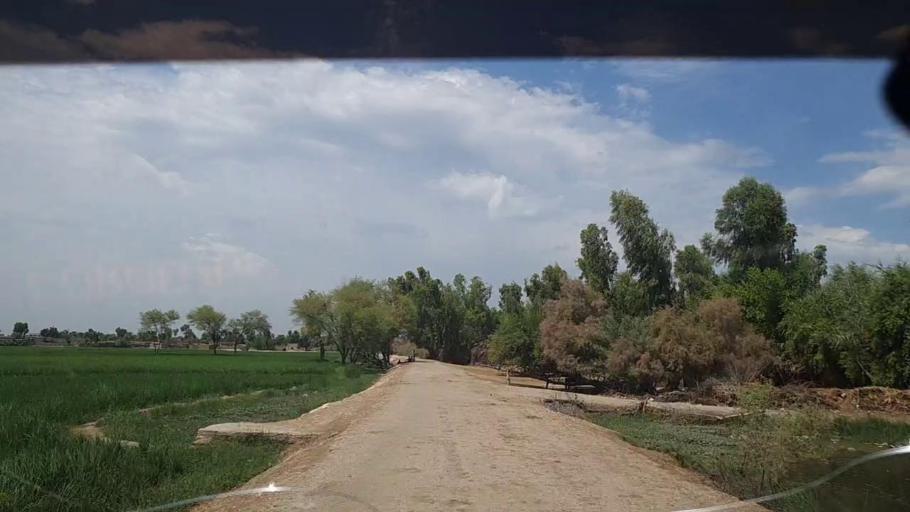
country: PK
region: Sindh
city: Ghauspur
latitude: 28.1514
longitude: 68.9975
